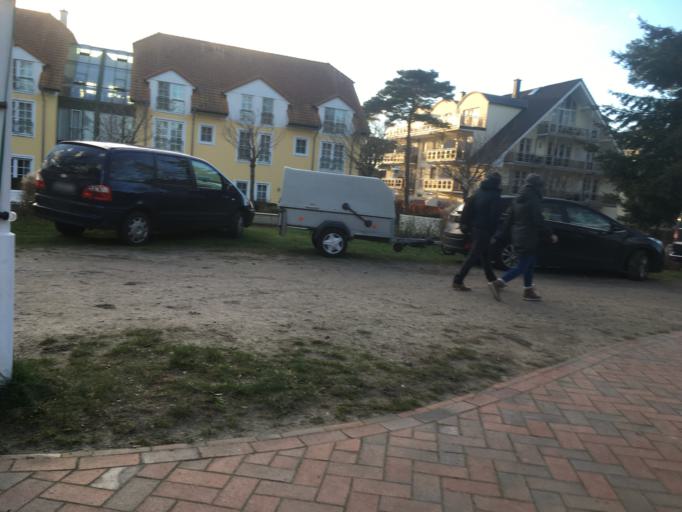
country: DE
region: Mecklenburg-Vorpommern
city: Ostseebad Sellin
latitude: 54.3626
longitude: 13.7140
